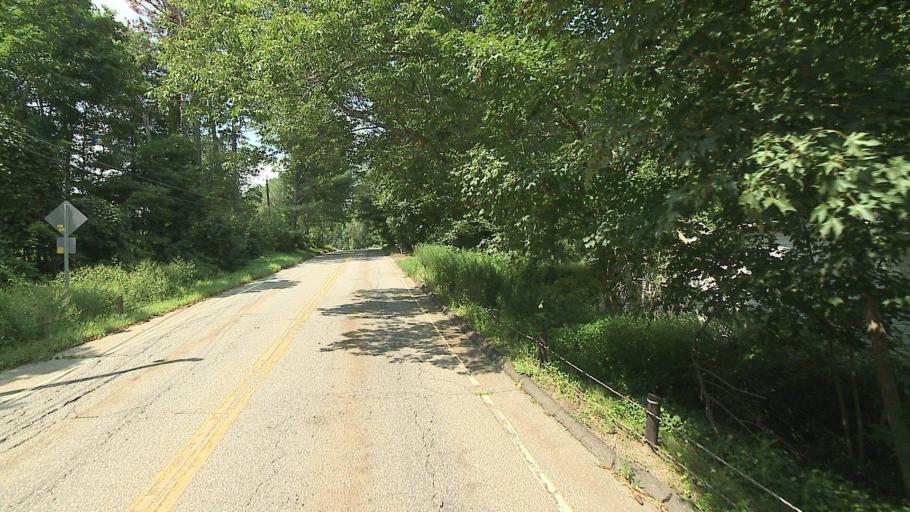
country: US
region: Connecticut
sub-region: Litchfield County
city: Bethlehem Village
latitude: 41.6741
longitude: -73.1571
